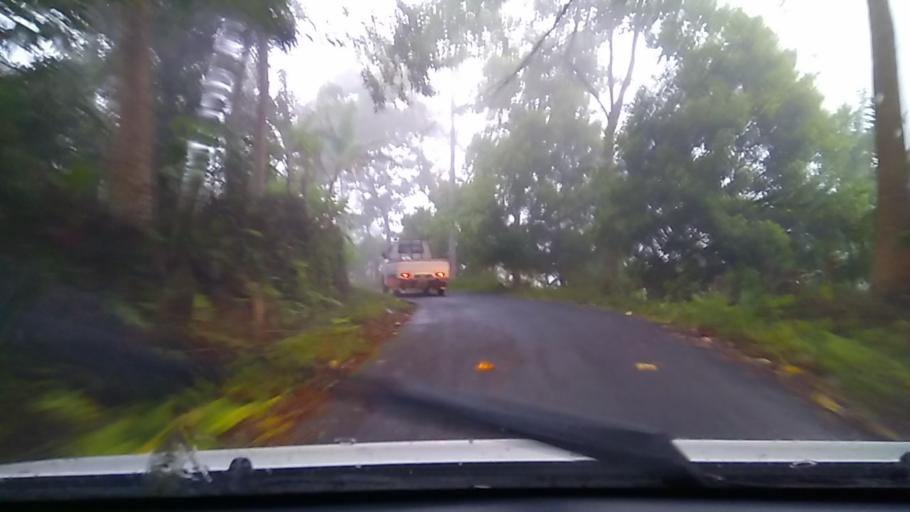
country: ID
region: Bali
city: Banjar Ambengan
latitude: -8.2056
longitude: 115.1724
